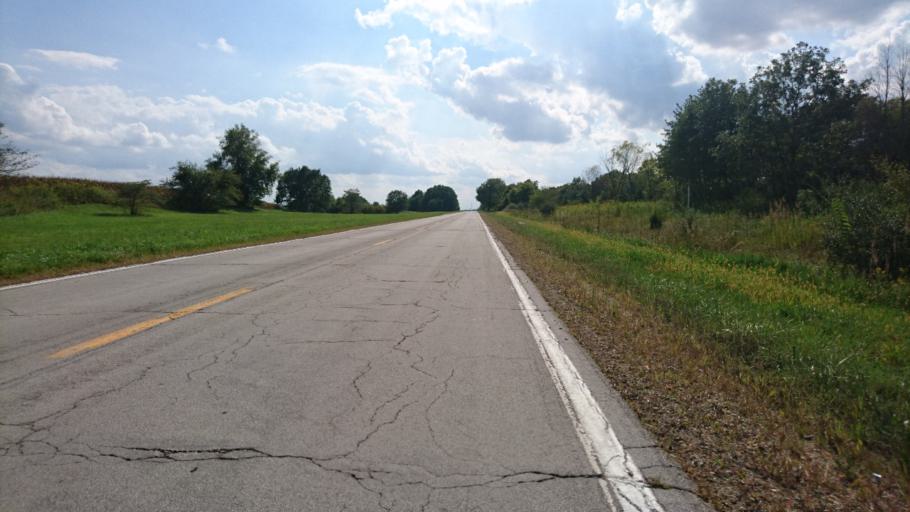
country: US
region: Illinois
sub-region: Logan County
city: Atlanta
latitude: 40.3482
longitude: -89.1300
